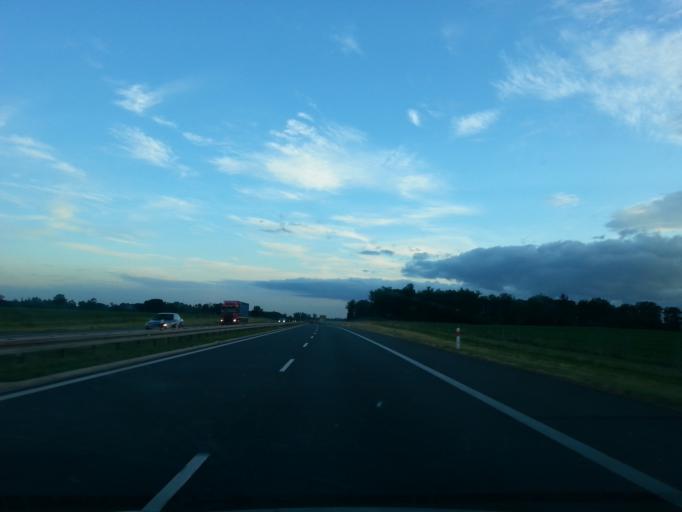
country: PL
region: Lower Silesian Voivodeship
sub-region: Powiat olesnicki
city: Twardogora
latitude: 51.2720
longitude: 17.5558
